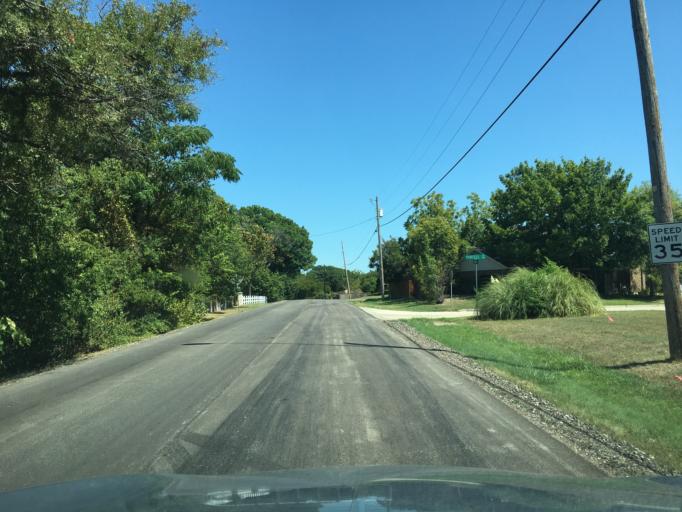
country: US
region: Texas
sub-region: Dallas County
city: Garland
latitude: 32.9519
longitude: -96.6359
